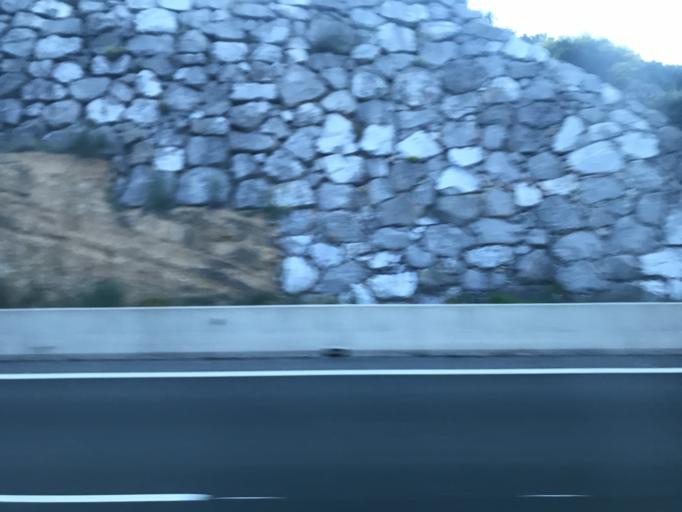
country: ES
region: Basque Country
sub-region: Provincia de Alava
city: Arminon
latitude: 42.7842
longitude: -2.8237
